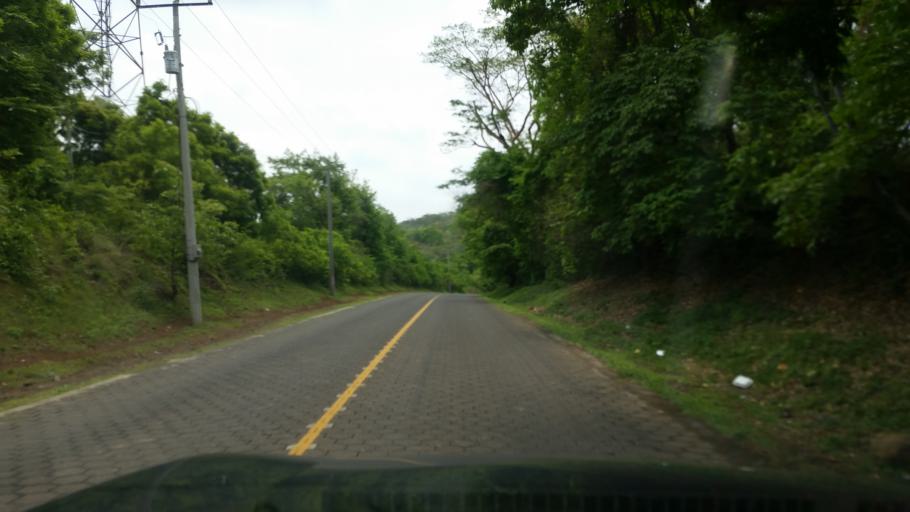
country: NI
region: Managua
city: Masachapa
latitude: 11.8585
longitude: -86.5191
